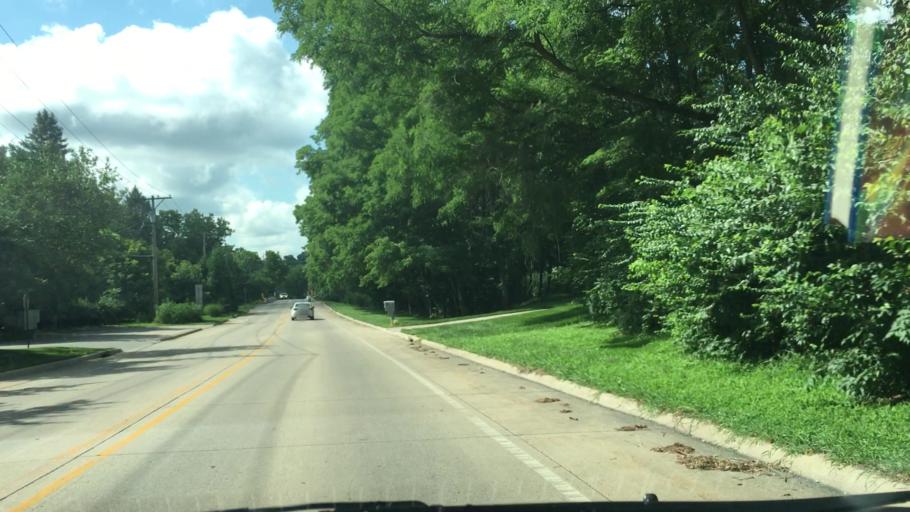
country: US
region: Iowa
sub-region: Johnson County
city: Iowa City
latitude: 41.6891
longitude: -91.5250
